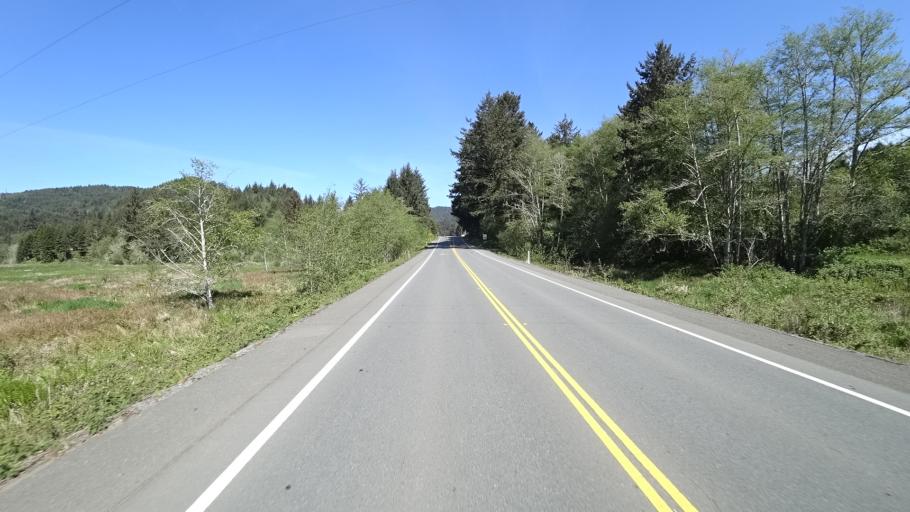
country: US
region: California
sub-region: Del Norte County
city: Bertsch-Oceanview
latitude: 41.5709
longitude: -124.0705
